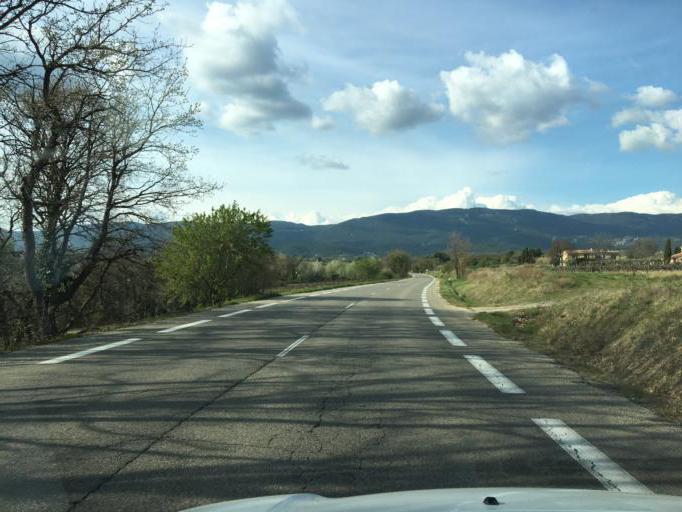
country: FR
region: Provence-Alpes-Cote d'Azur
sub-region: Departement du Vaucluse
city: Ansouis
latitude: 43.7522
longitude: 5.4610
